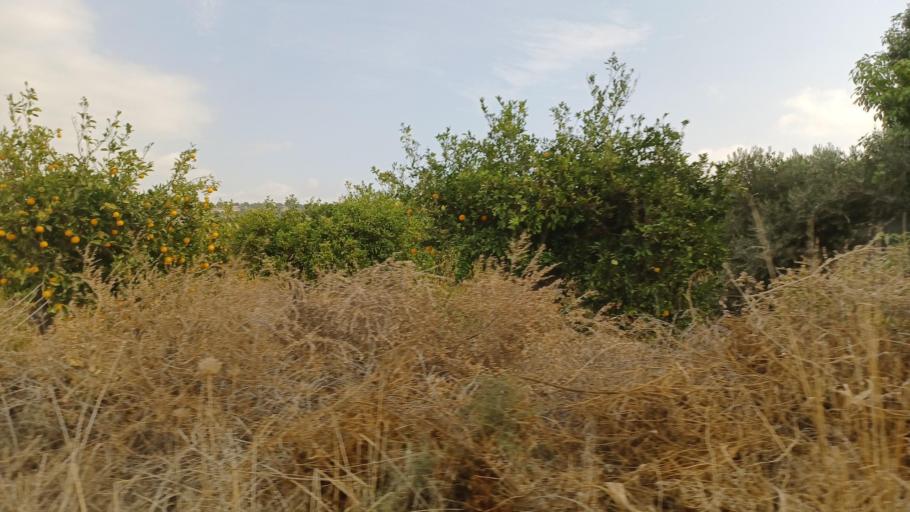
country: CY
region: Pafos
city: Pegeia
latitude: 34.8960
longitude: 32.3351
